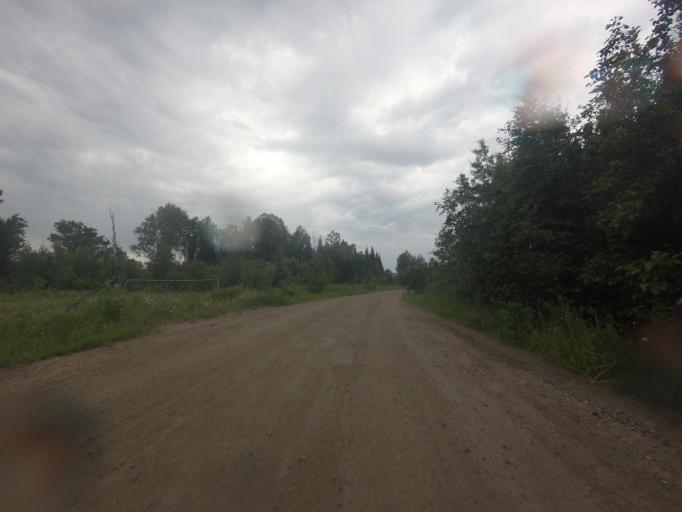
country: CA
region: Quebec
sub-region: Outaouais
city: Maniwaki
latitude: 46.4480
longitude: -75.9374
